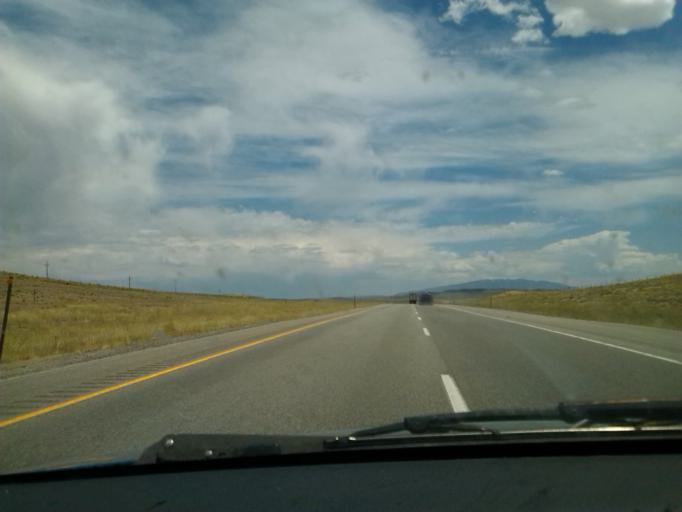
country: US
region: Wyoming
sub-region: Carbon County
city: Rawlins
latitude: 41.7569
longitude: -106.9776
